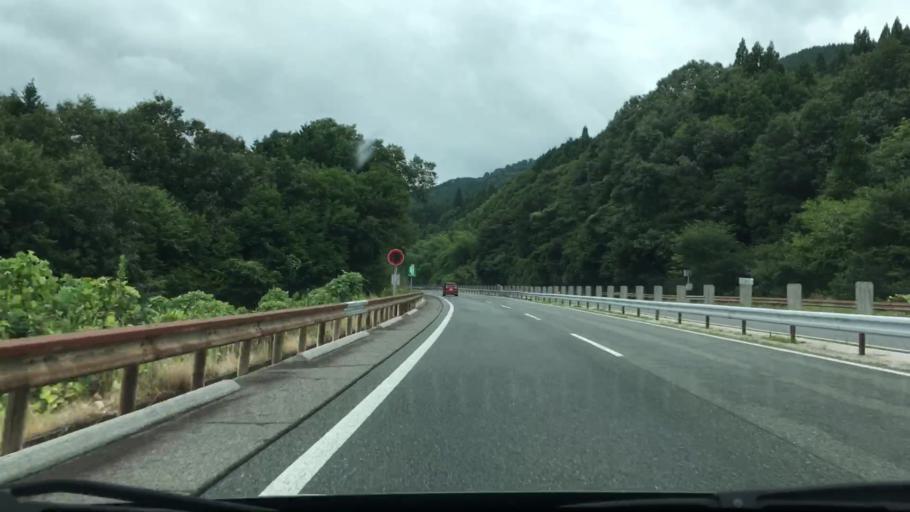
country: JP
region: Okayama
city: Niimi
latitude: 34.9579
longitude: 133.3298
